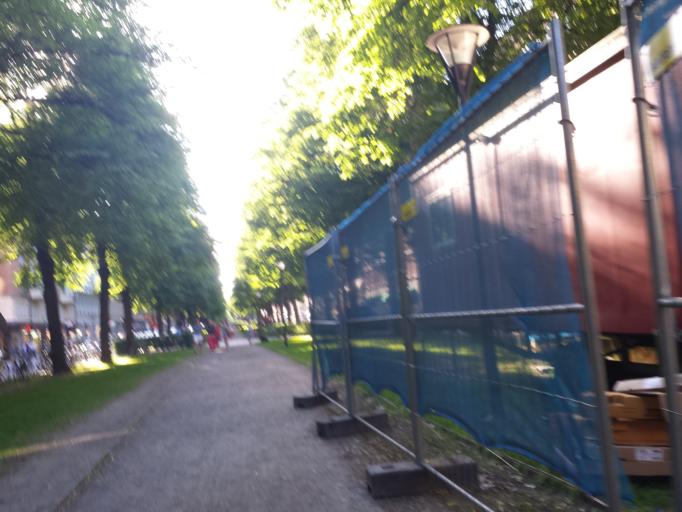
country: SE
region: Stockholm
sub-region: Stockholms Kommun
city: OEstermalm
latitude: 59.3394
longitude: 18.0821
